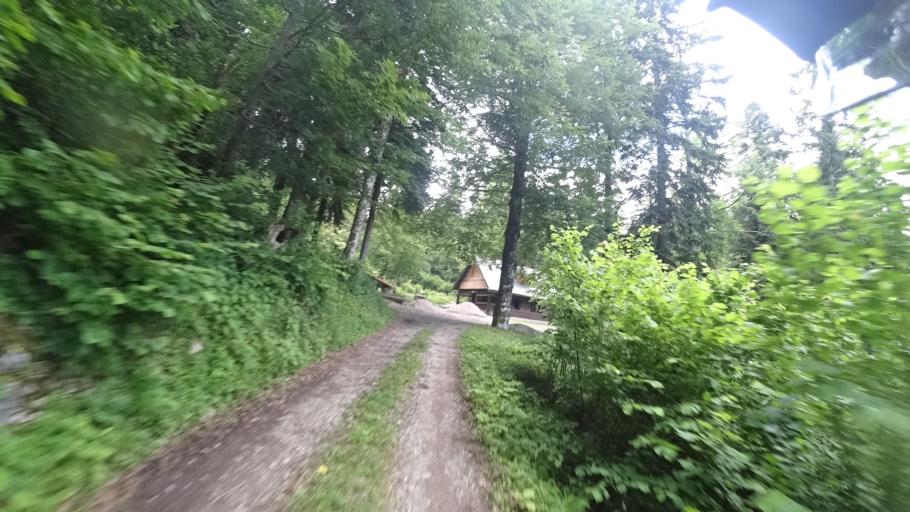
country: SI
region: Osilnica
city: Osilnica
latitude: 45.4856
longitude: 14.6781
